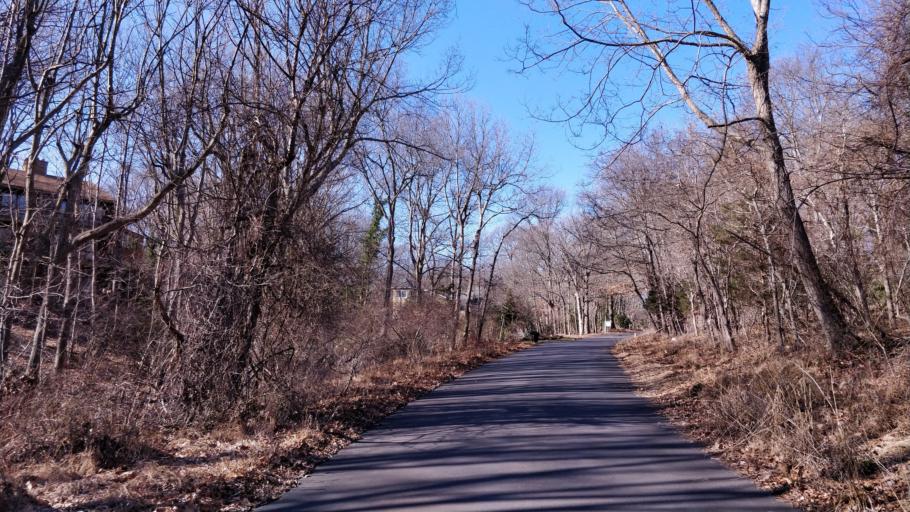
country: US
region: New York
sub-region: Suffolk County
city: Port Jefferson
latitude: 40.9658
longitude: -73.0612
